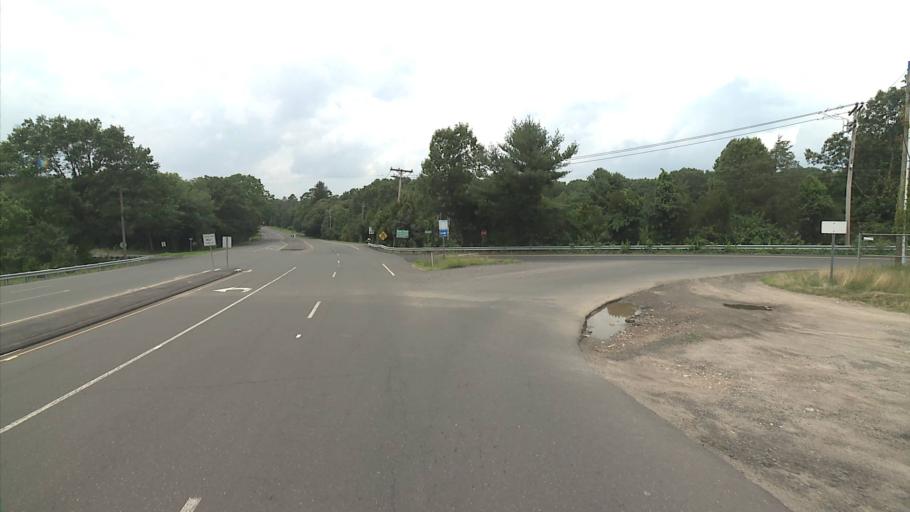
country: US
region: Connecticut
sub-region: New Haven County
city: Madison
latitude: 41.2918
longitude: -72.5709
